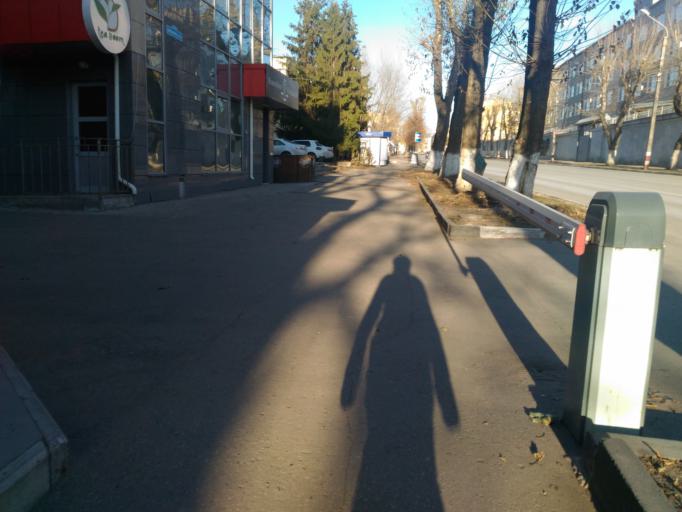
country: RU
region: Ulyanovsk
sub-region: Ulyanovskiy Rayon
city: Ulyanovsk
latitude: 54.3199
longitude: 48.3857
